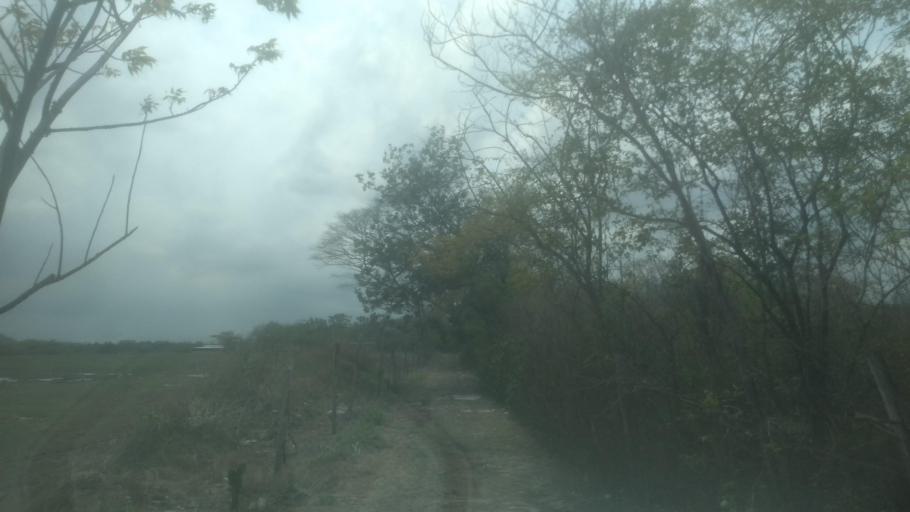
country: MX
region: Veracruz
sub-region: Emiliano Zapata
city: Plan del Rio
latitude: 19.3871
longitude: -96.6261
